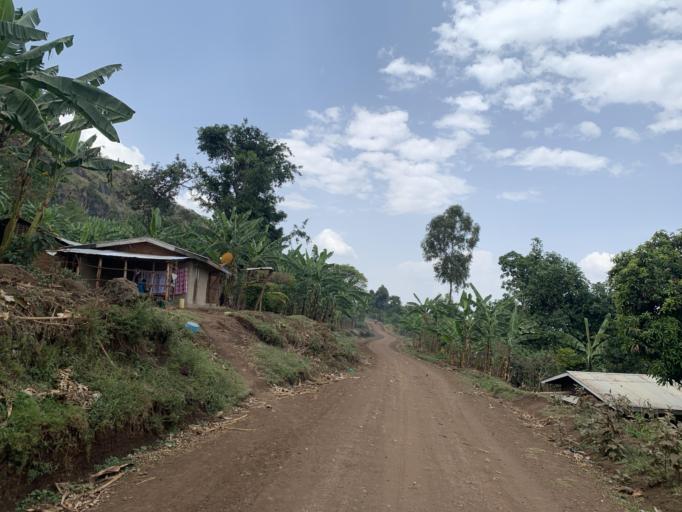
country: UG
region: Eastern Region
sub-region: Sironko District
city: Sironko
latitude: 1.2571
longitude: 34.3104
